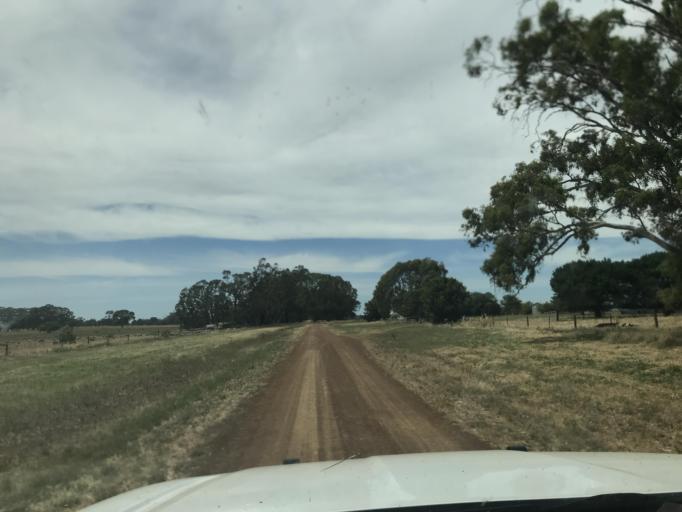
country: AU
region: South Australia
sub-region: Wattle Range
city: Penola
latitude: -37.0266
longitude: 141.4911
